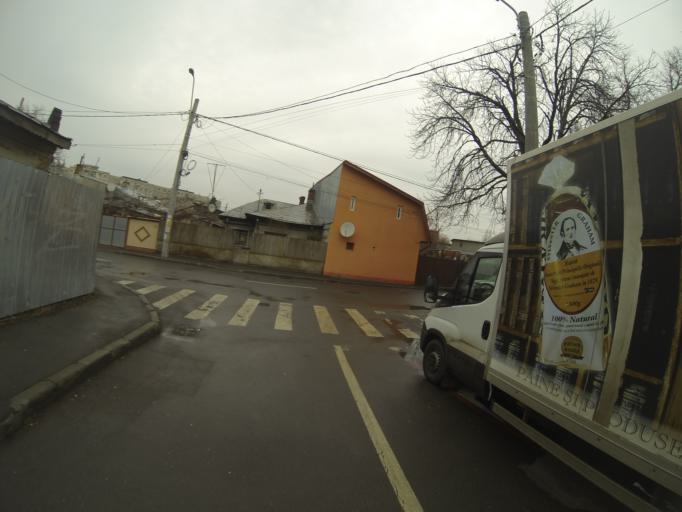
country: RO
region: Bucuresti
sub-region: Municipiul Bucuresti
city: Bucuresti
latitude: 44.4013
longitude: 26.0758
